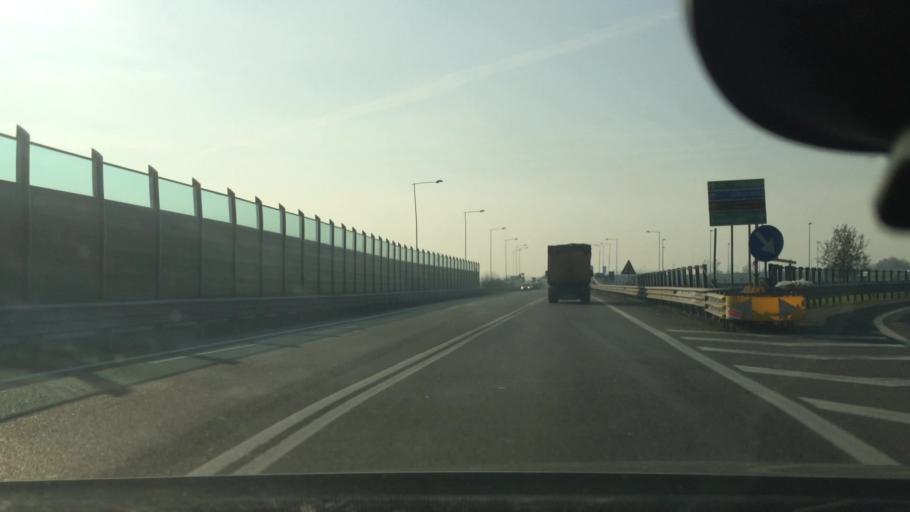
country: IT
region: Lombardy
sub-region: Provincia di Varese
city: Origgio
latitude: 45.6096
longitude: 9.0164
